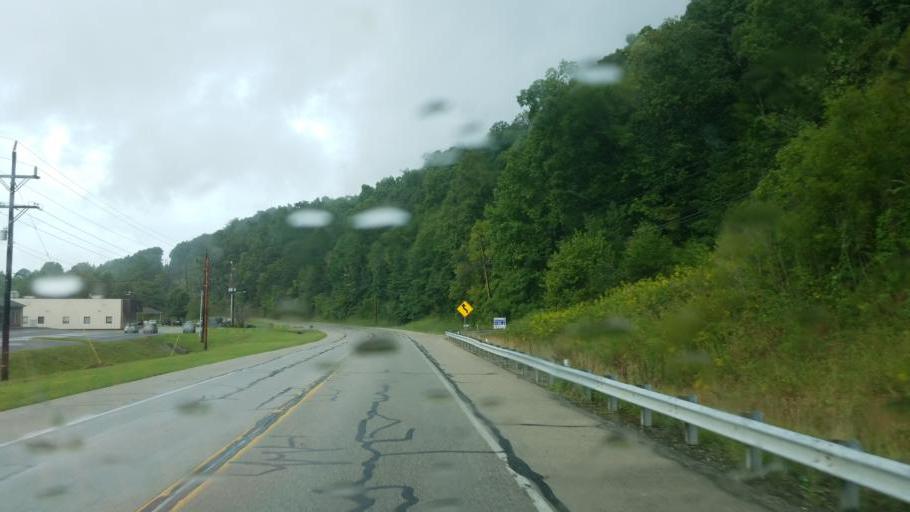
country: US
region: Kentucky
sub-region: Rowan County
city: Morehead
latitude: 38.1667
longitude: -83.4436
